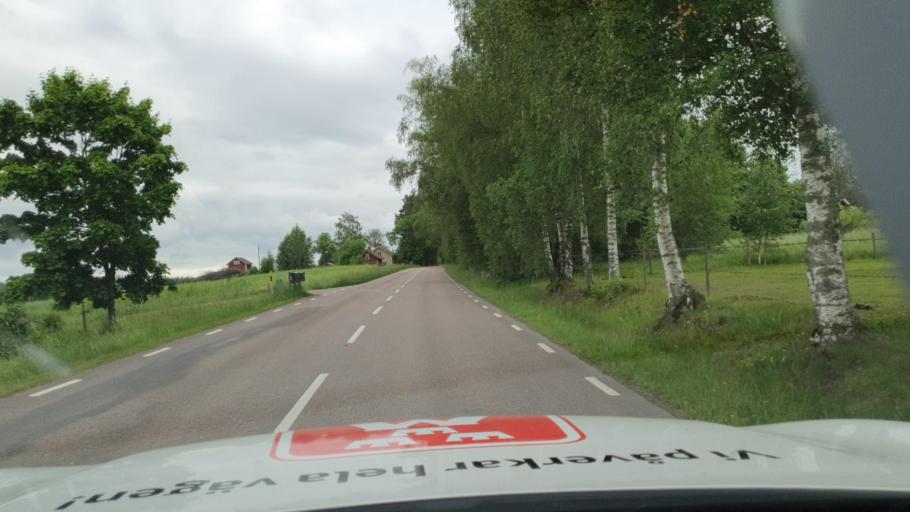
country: SE
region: Vaermland
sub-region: Kils Kommun
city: Kil
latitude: 59.5323
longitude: 13.3146
